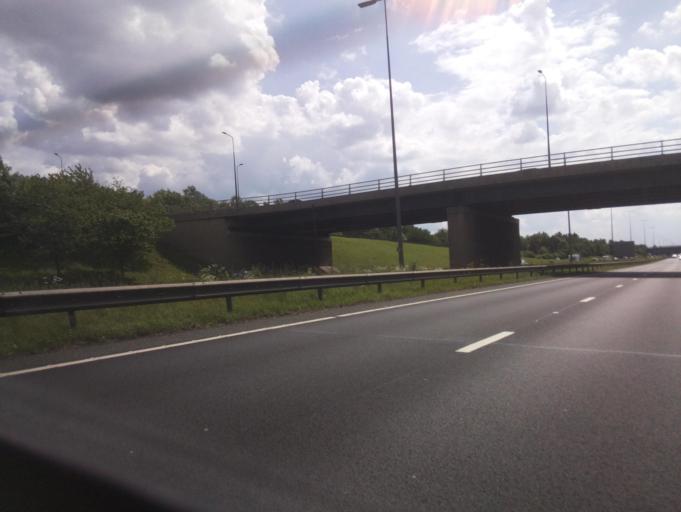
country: GB
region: England
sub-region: Redcar and Cleveland
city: Thornaby-on-Tees
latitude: 54.5486
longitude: -1.2751
